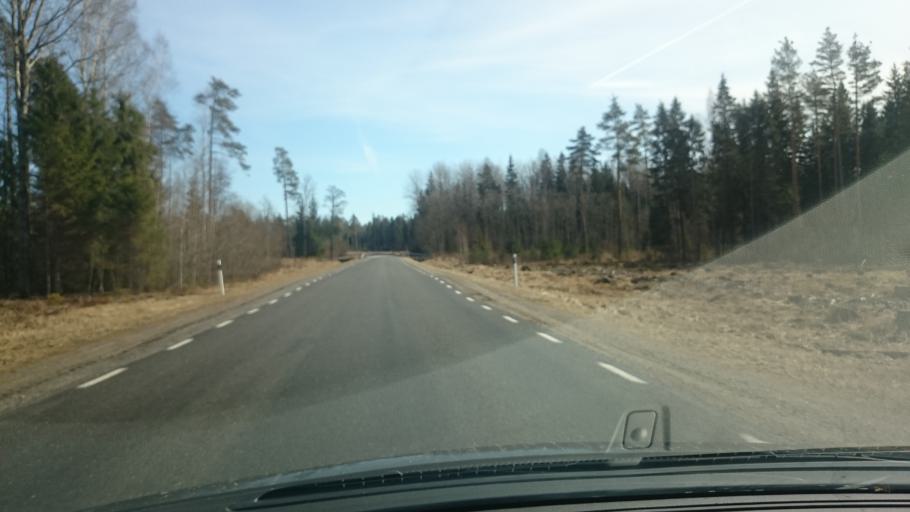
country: EE
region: Paernumaa
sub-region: Tootsi vald
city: Tootsi
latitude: 58.6428
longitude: 24.8864
